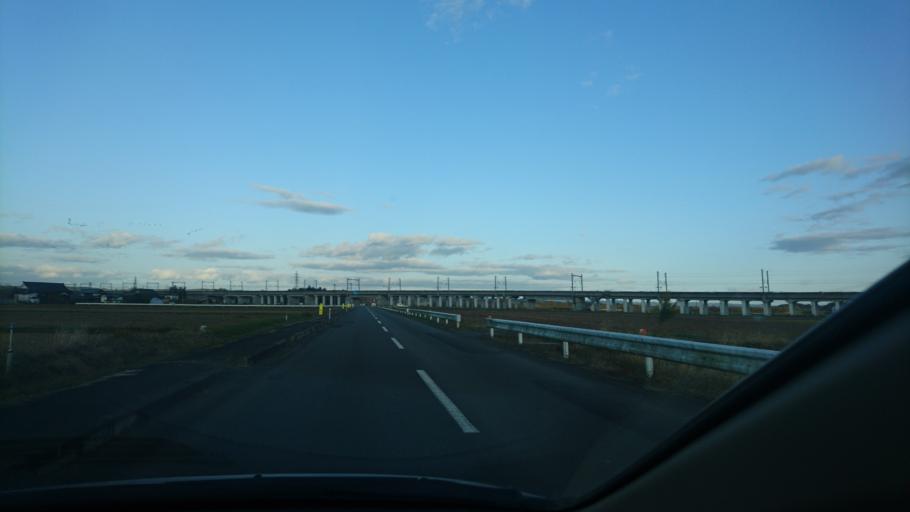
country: JP
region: Iwate
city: Ichinoseki
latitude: 38.7814
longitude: 141.0867
